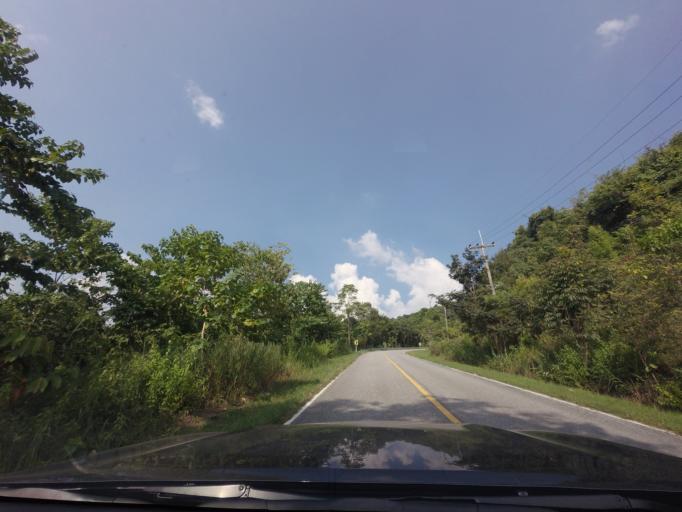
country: TH
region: Phitsanulok
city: Nakhon Thai
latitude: 17.0203
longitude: 100.9707
